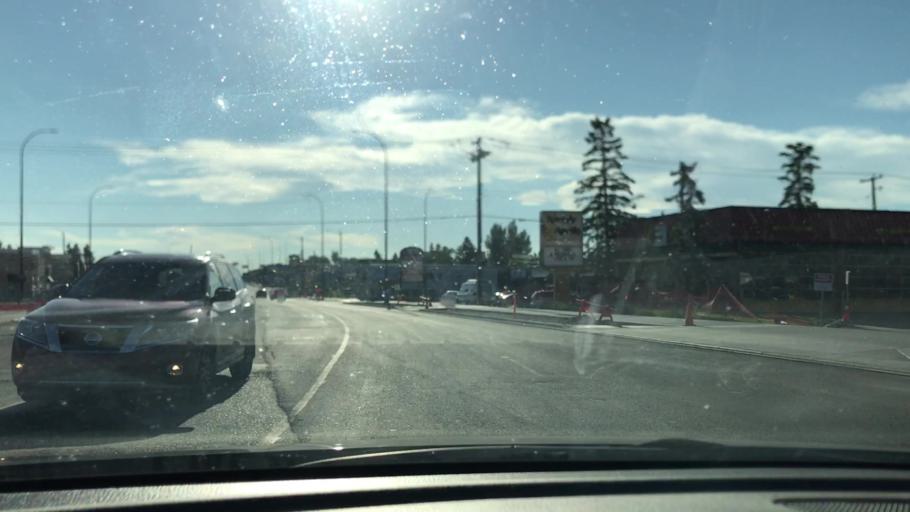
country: CA
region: Alberta
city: Calgary
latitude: 51.0379
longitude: -113.9670
